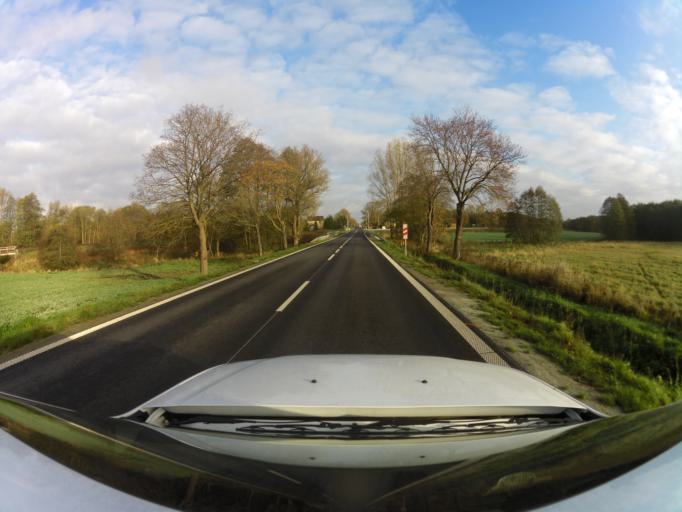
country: PL
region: West Pomeranian Voivodeship
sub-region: Powiat gryficki
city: Gryfice
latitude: 53.9673
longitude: 15.2313
